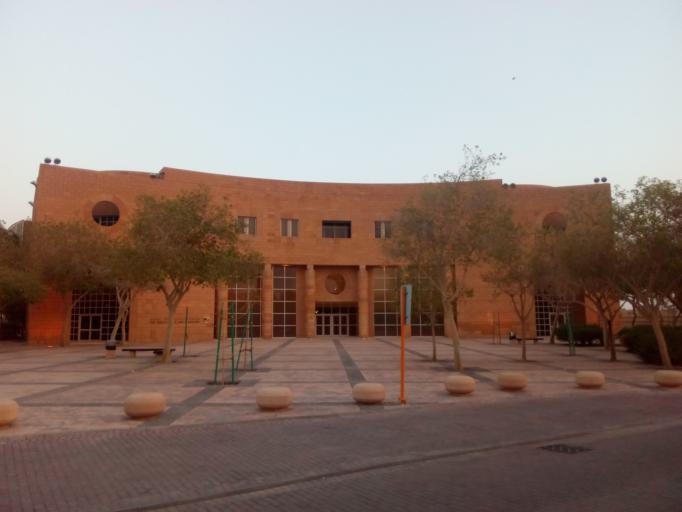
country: SA
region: Ar Riyad
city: Riyadh
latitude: 24.6437
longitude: 46.7107
